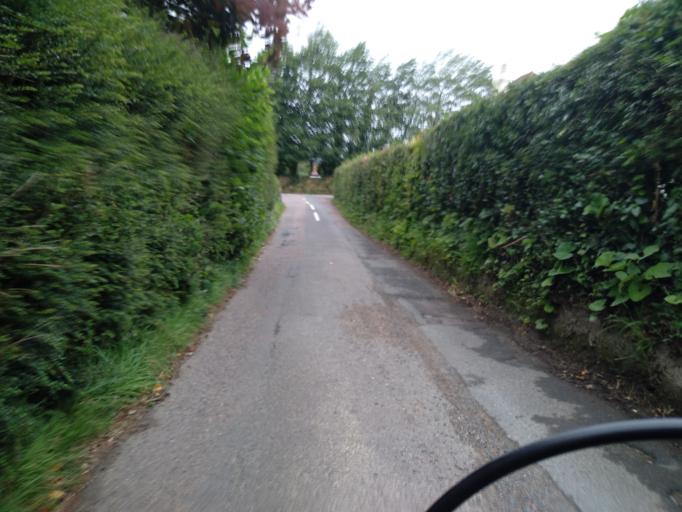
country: GB
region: England
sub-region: Isle of Wight
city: Sandown
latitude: 50.6656
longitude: -1.1697
